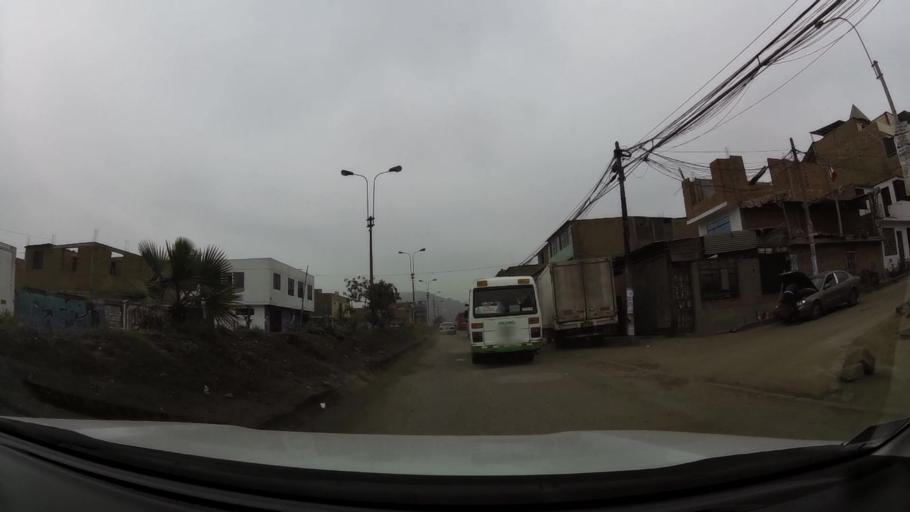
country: PE
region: Lima
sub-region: Lima
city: Surco
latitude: -12.1692
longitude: -76.9615
